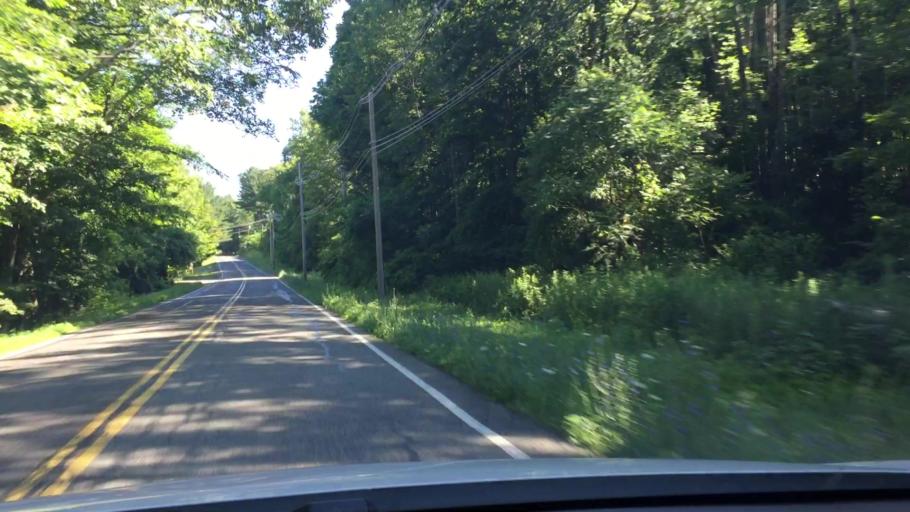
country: US
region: Massachusetts
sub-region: Berkshire County
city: West Stockbridge
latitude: 42.3414
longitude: -73.3663
